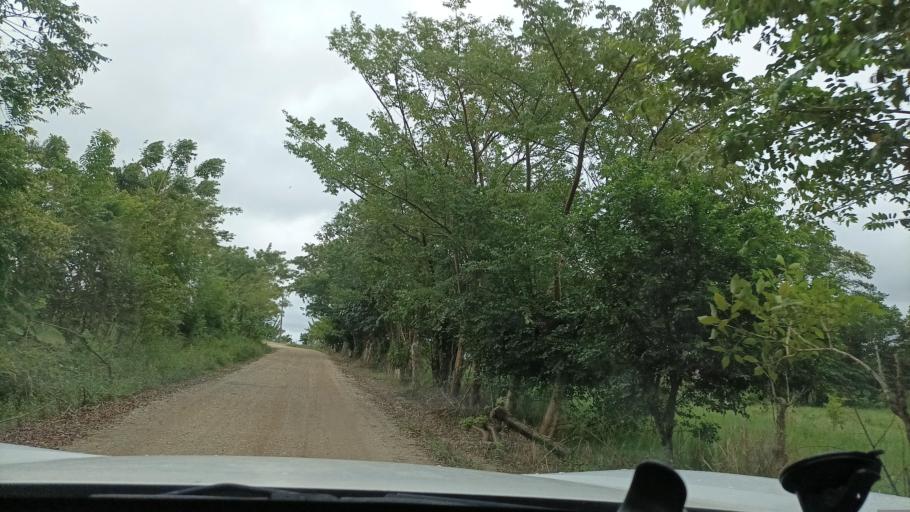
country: MX
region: Veracruz
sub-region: Moloacan
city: Cuichapa
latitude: 17.7882
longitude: -94.3564
